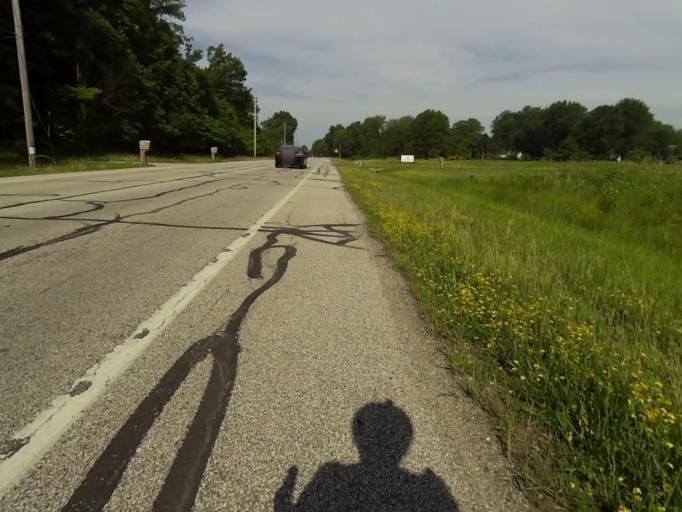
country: US
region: Ohio
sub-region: Summit County
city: Hudson
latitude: 41.2180
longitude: -81.4618
